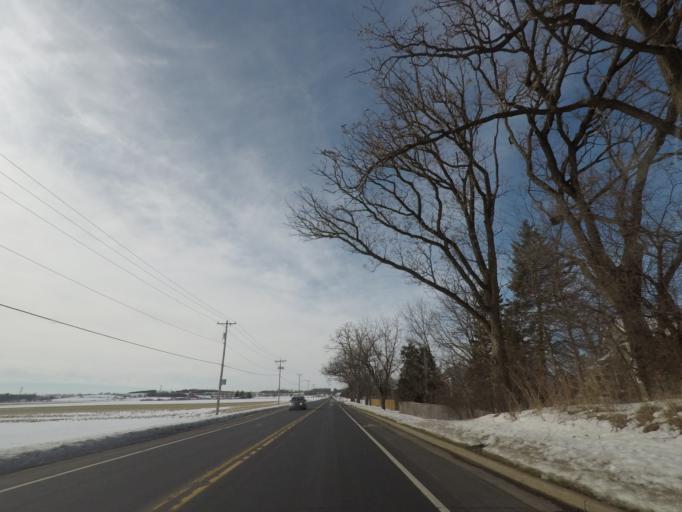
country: US
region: Wisconsin
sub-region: Dane County
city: Fitchburg
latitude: 43.0013
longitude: -89.4467
